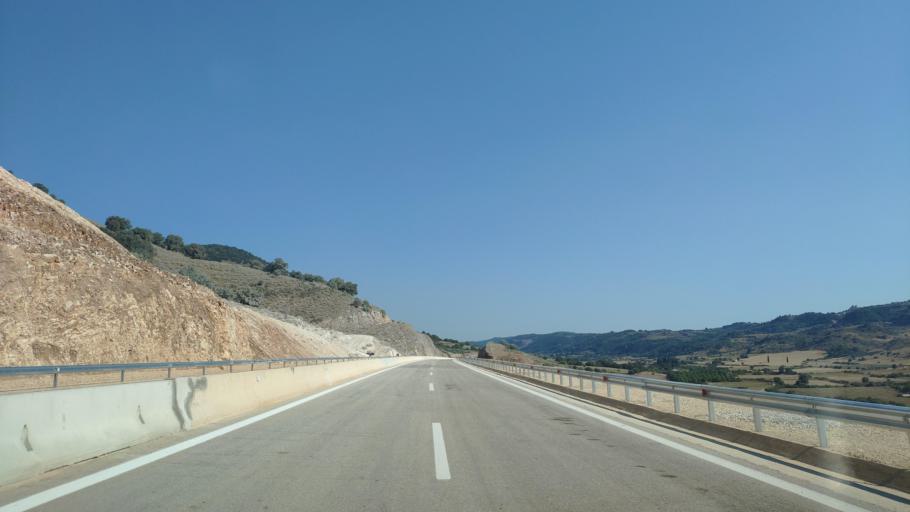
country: GR
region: West Greece
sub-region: Nomos Aitolias kai Akarnanias
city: Katouna
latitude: 38.8223
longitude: 21.1248
